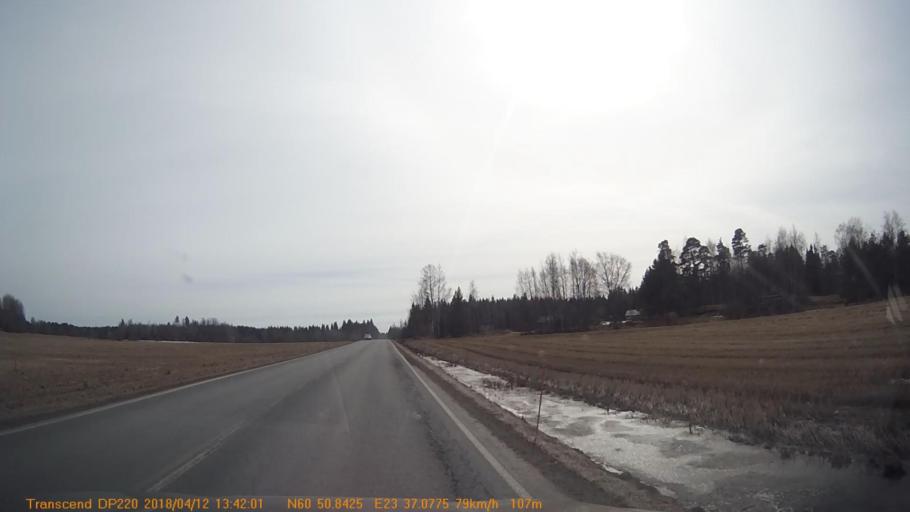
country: FI
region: Haeme
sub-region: Forssa
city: Forssa
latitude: 60.8466
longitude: 23.6180
